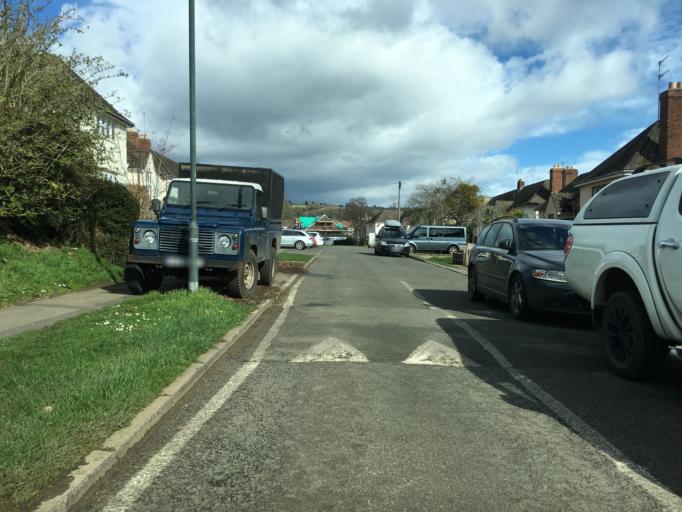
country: GB
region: England
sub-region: Gloucestershire
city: Wotton-under-Edge
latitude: 51.6360
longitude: -2.3452
